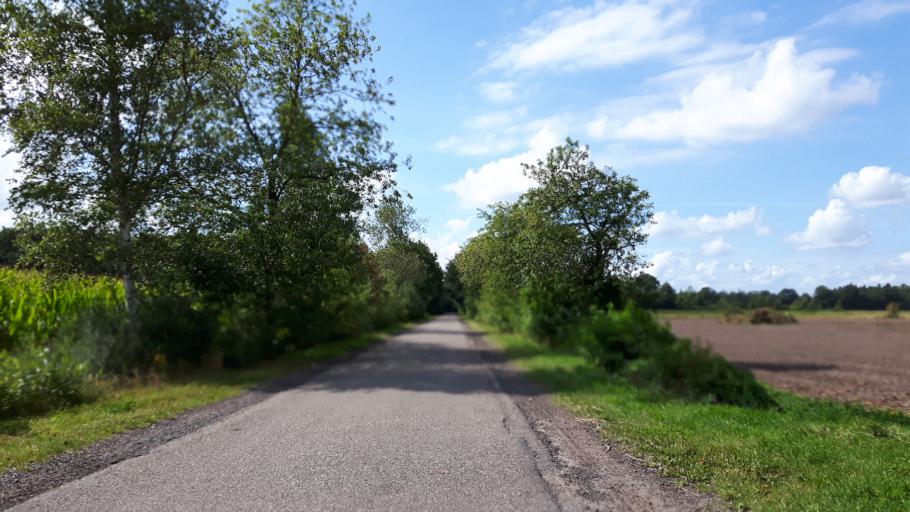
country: NL
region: Groningen
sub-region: Gemeente Leek
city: Leek
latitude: 53.0849
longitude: 6.2992
